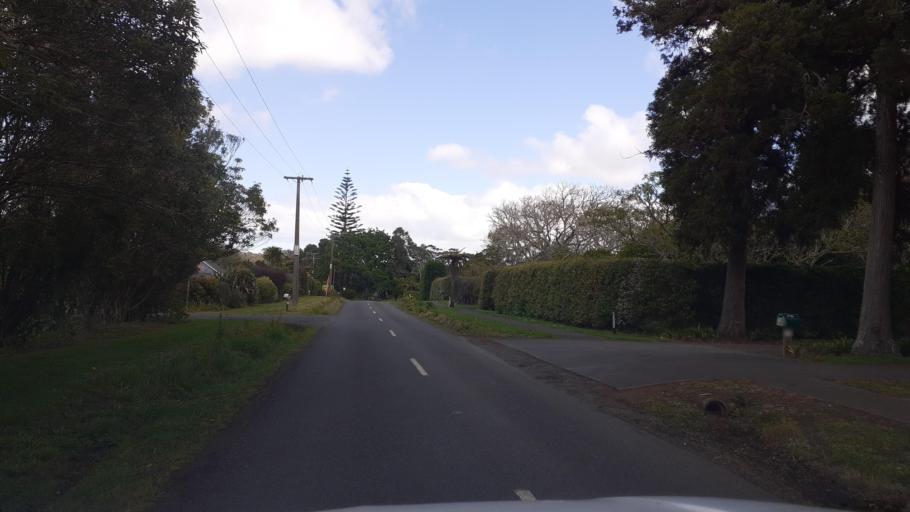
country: NZ
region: Northland
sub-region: Far North District
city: Kerikeri
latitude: -35.2424
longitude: 173.9569
